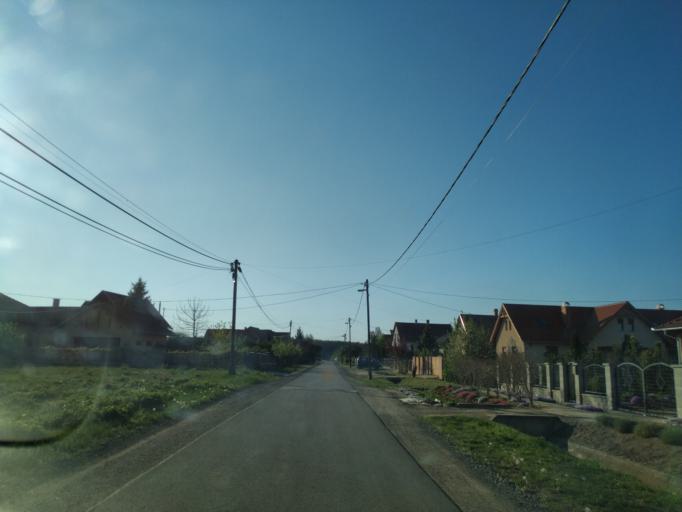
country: HU
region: Pest
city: Nagykata
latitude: 47.4214
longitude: 19.7253
